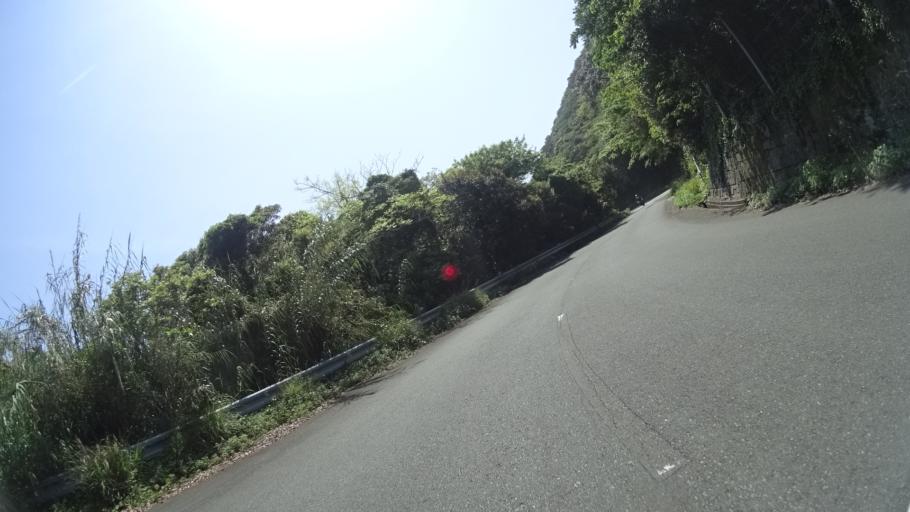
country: JP
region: Oita
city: Tsukumiura
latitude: 33.3582
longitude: 132.0337
